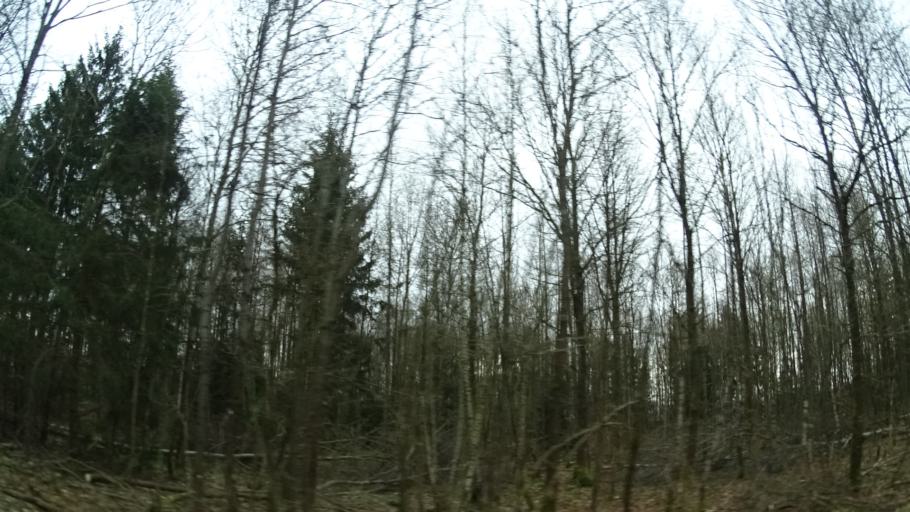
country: DE
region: Rheinland-Pfalz
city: Ippenschied
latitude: 49.8845
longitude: 7.6244
